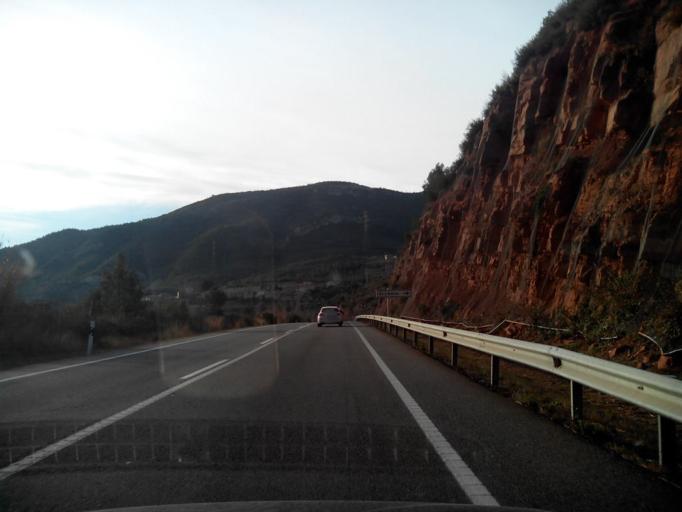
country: ES
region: Catalonia
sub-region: Provincia de Barcelona
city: Collbato
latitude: 41.5783
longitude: 1.8596
